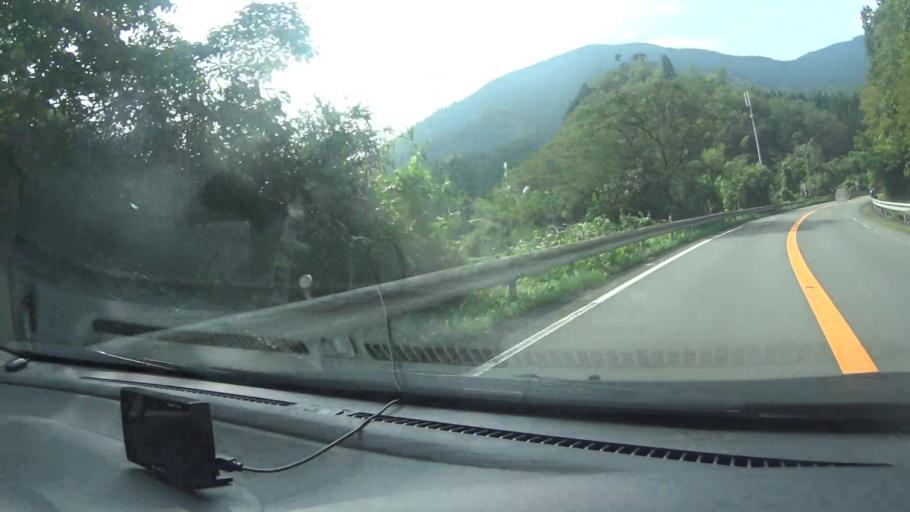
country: JP
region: Hyogo
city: Sasayama
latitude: 35.1456
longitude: 135.3550
